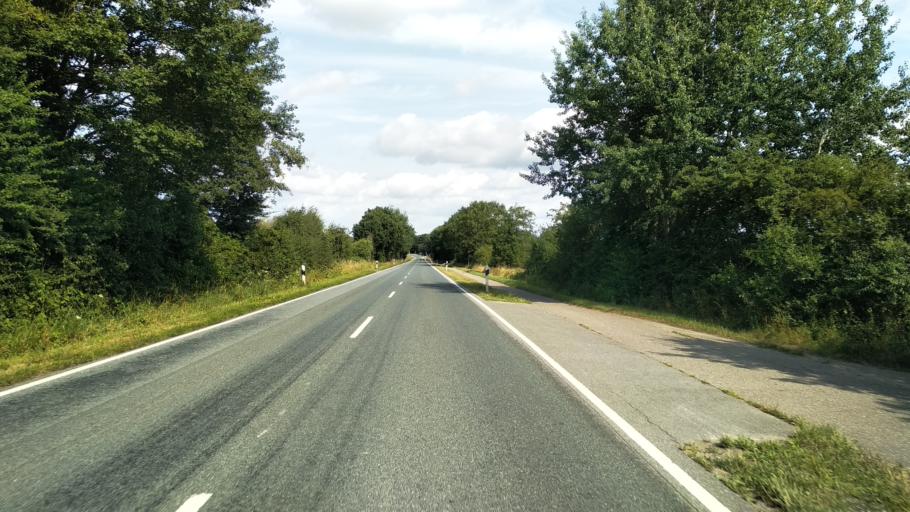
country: DE
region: Schleswig-Holstein
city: Selk
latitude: 54.4795
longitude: 9.5663
